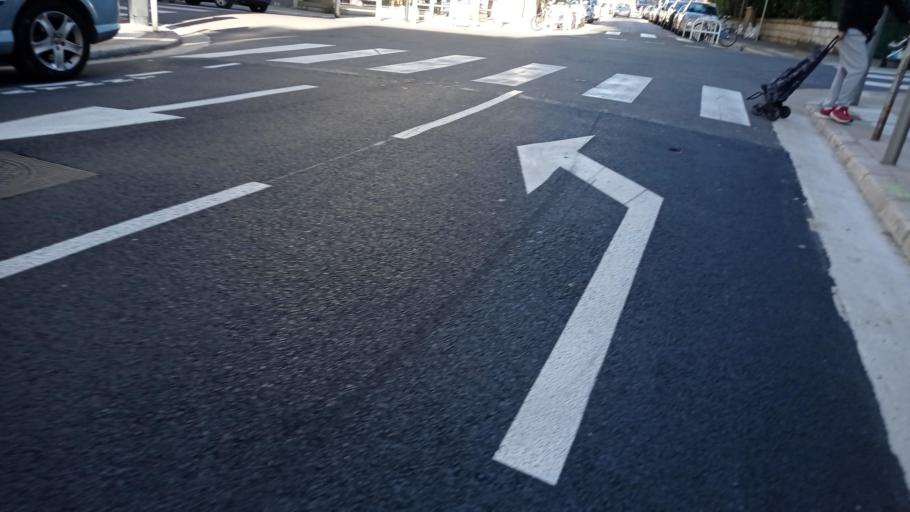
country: FR
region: Provence-Alpes-Cote d'Azur
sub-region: Departement des Alpes-Maritimes
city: Nice
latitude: 43.7015
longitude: 7.2617
